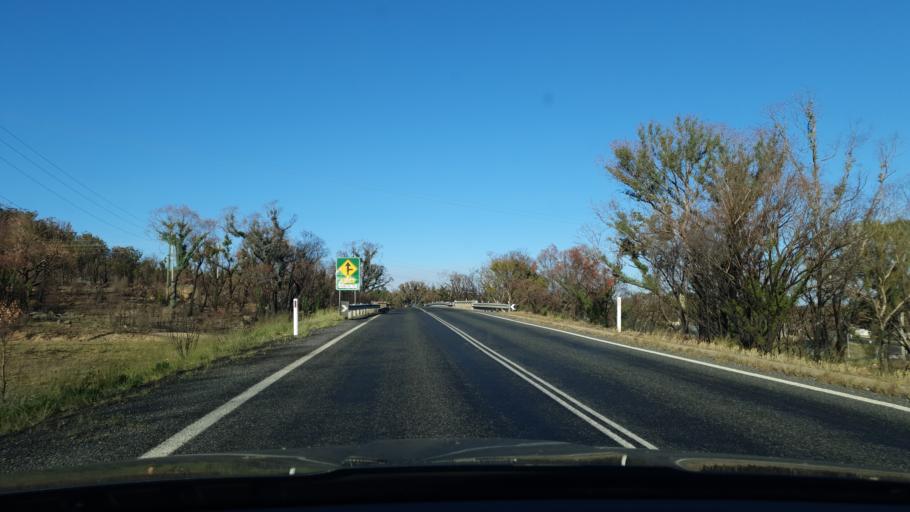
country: AU
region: Queensland
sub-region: Southern Downs
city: Stanthorpe
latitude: -28.6513
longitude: 151.9203
